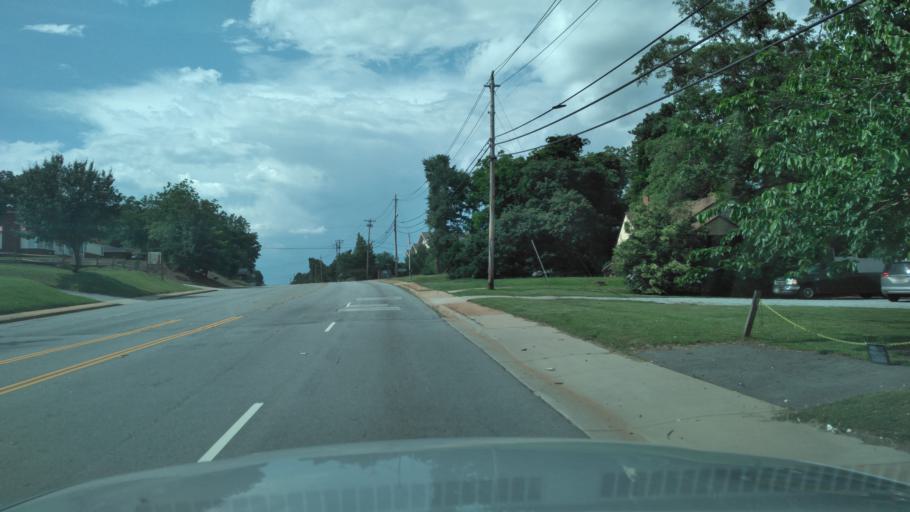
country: US
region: South Carolina
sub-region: Spartanburg County
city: Spartanburg
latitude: 34.9760
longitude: -81.9422
